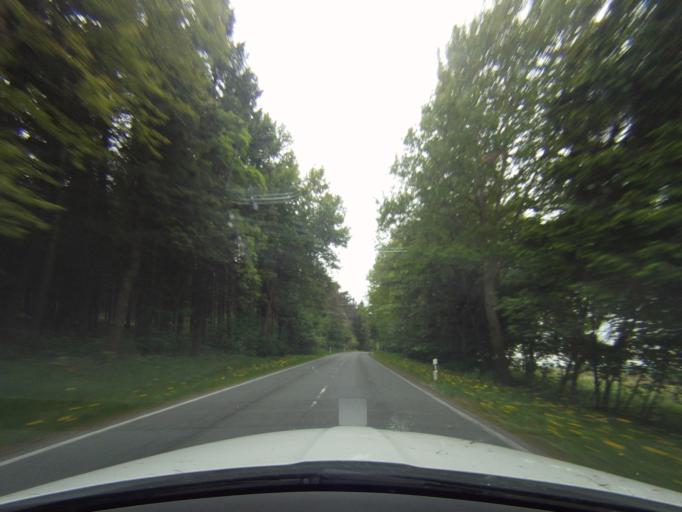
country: DE
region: Thuringia
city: Gillersdorf
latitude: 50.6157
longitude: 11.0261
